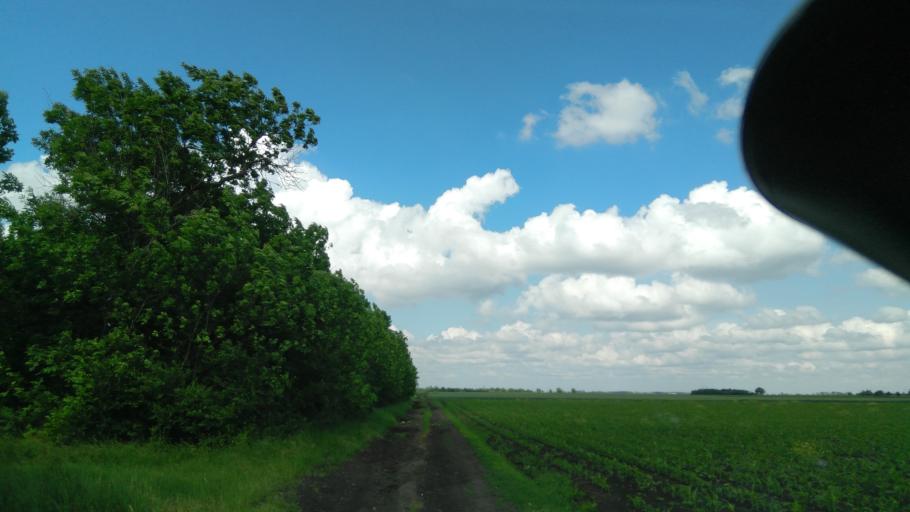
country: HU
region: Bekes
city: Mezobereny
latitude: 46.8343
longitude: 21.0076
